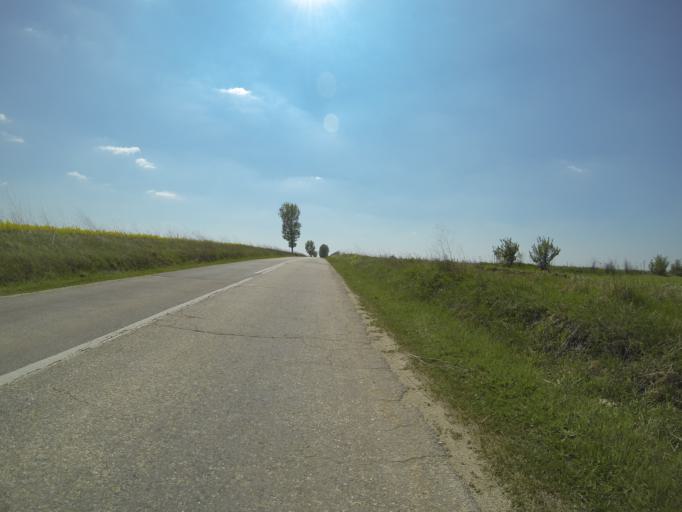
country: RO
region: Dolj
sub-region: Comuna Vartop
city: Vartop
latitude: 44.2084
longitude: 23.3016
